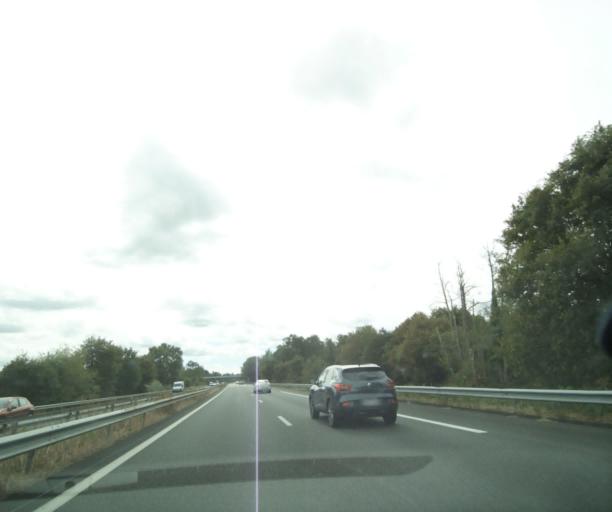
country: FR
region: Aquitaine
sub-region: Departement de la Gironde
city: Reignac
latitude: 45.2070
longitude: -0.5018
